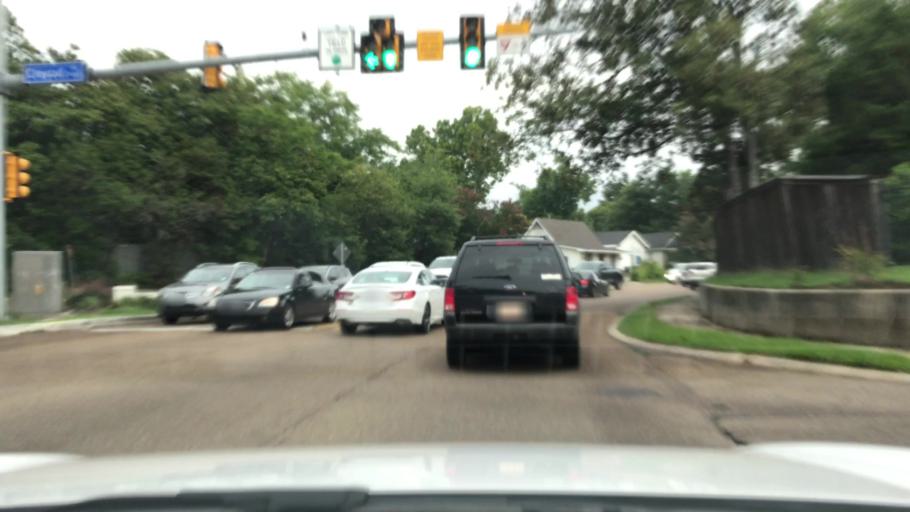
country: US
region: Louisiana
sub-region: East Baton Rouge Parish
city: Baton Rouge
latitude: 30.4413
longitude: -91.1382
